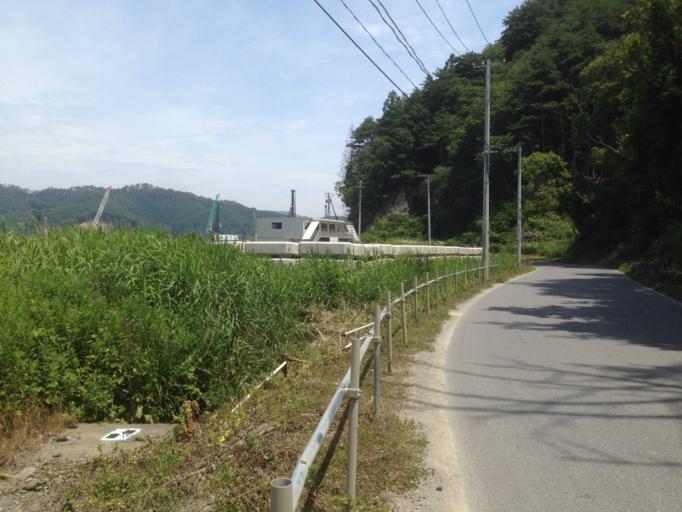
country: JP
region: Iwate
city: Otsuchi
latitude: 39.3283
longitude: 141.8956
